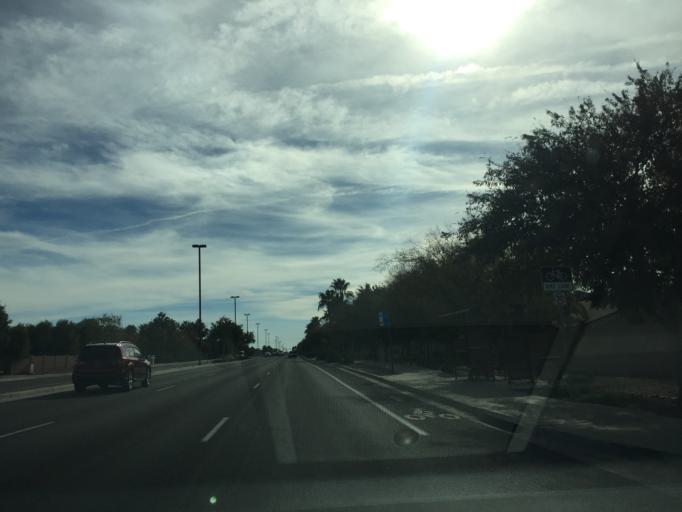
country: US
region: Arizona
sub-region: Maricopa County
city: Gilbert
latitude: 33.3272
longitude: -111.7899
